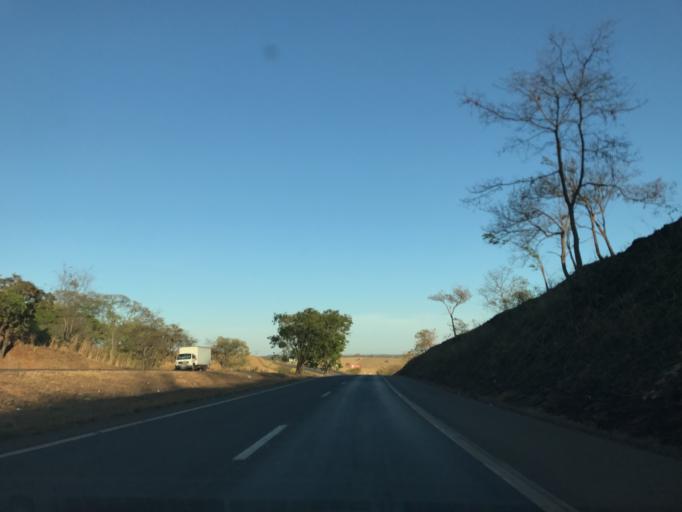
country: BR
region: Goias
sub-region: Goianapolis
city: Goianapolis
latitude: -16.4509
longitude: -49.0401
